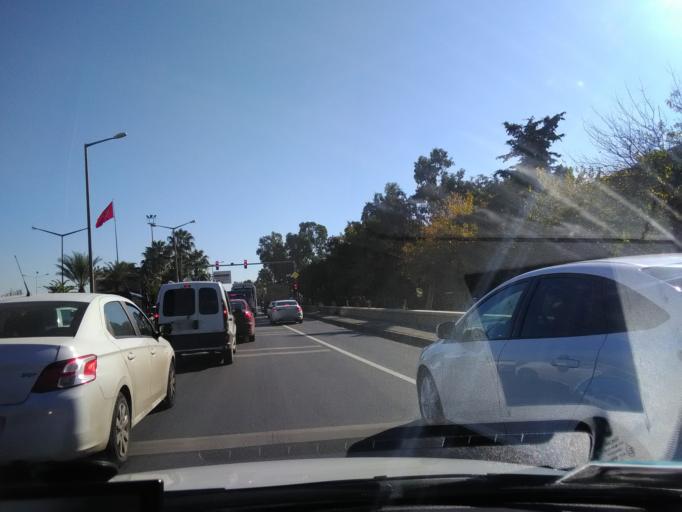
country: TR
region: Antalya
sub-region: Alanya
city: Mahmutlar
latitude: 36.5180
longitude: 32.0604
